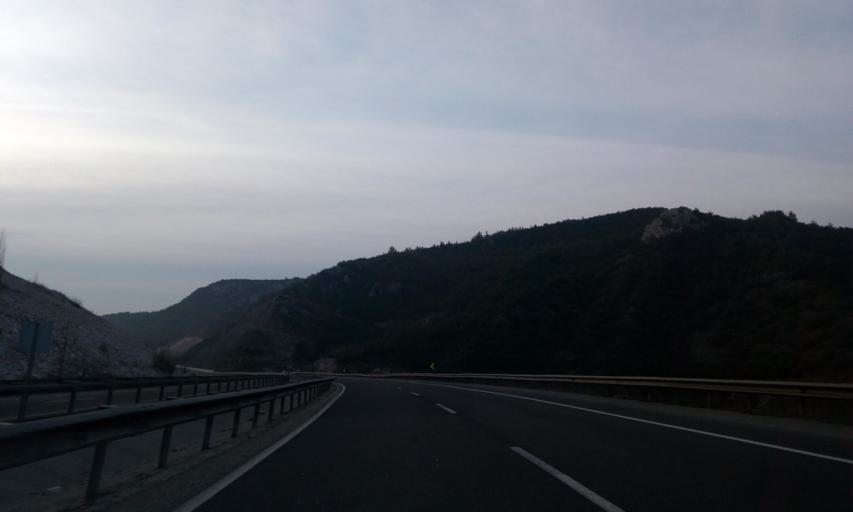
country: TR
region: Bilecik
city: Bilecik
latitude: 40.1577
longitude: 30.0185
